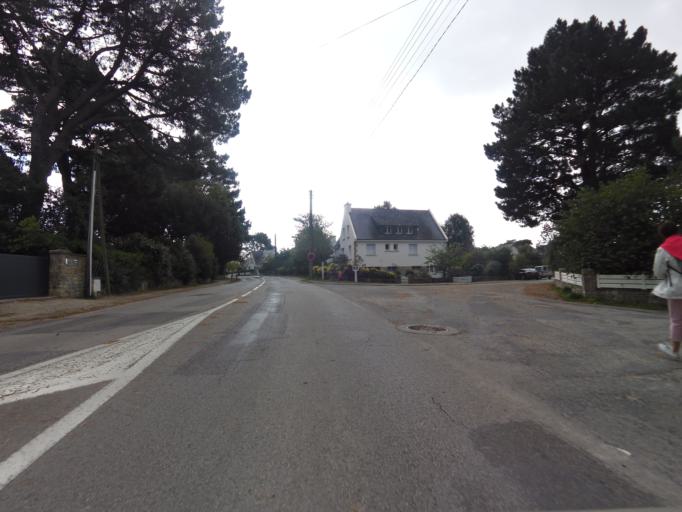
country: FR
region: Brittany
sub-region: Departement du Morbihan
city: Carnac
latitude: 47.5756
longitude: -3.0736
